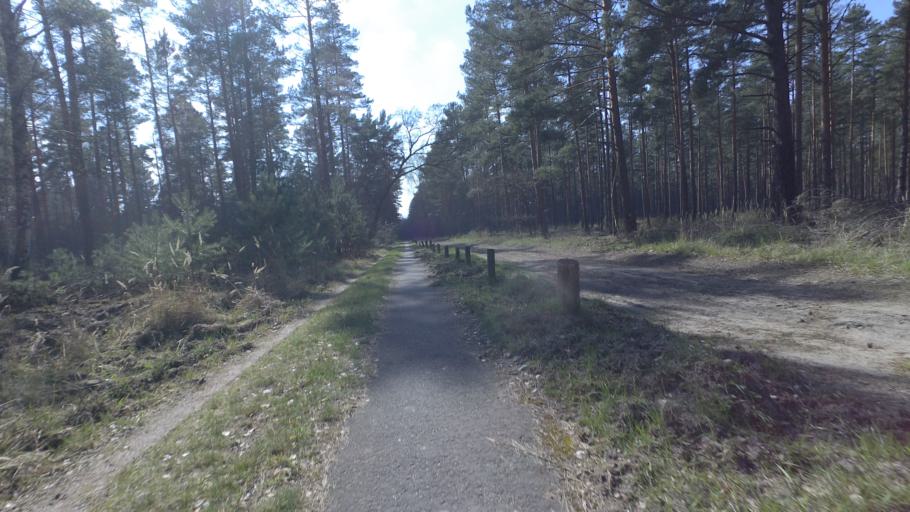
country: DE
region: Brandenburg
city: Mittenwalde
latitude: 52.1930
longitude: 13.5307
